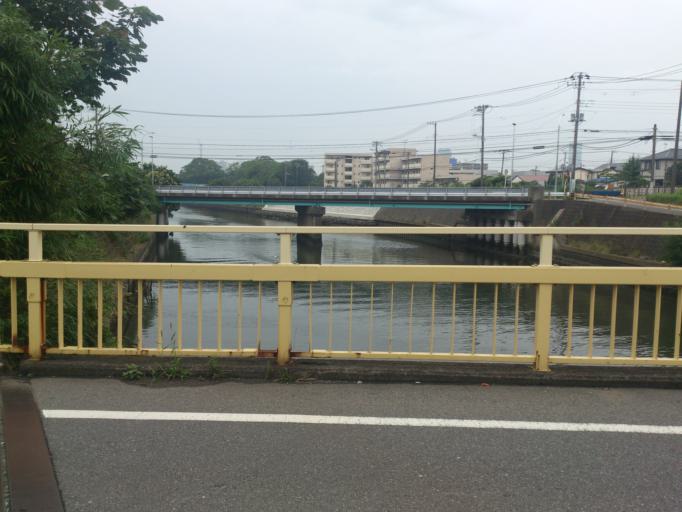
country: JP
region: Chiba
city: Chiba
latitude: 35.6534
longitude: 140.0626
